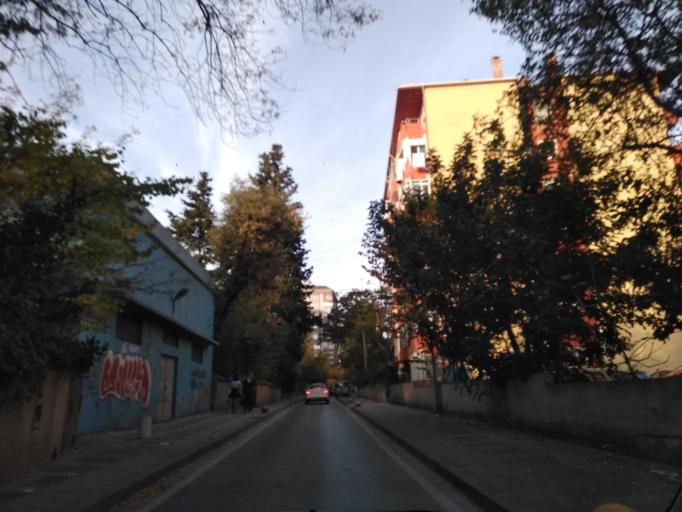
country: TR
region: Istanbul
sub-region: Atasehir
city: Atasehir
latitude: 40.9760
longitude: 29.0904
